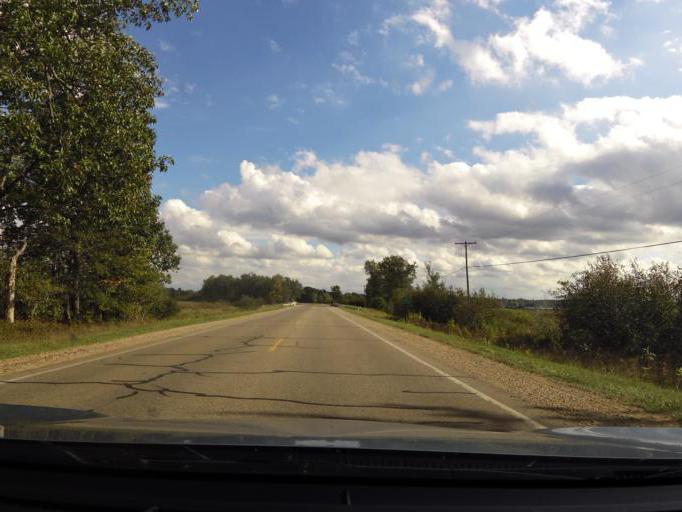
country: US
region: Michigan
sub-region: Roscommon County
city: Saint Helen
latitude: 44.3842
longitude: -84.4265
